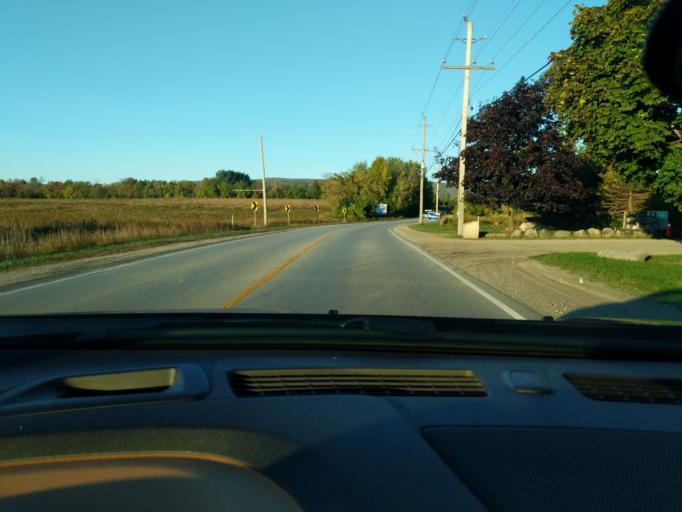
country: CA
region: Ontario
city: Collingwood
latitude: 44.4989
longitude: -80.2543
